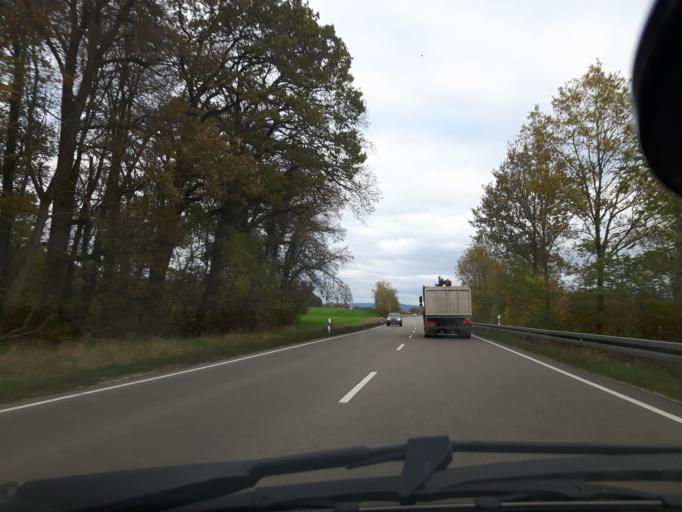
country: DE
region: Bavaria
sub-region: Regierungsbezirk Mittelfranken
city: Weidenbach
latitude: 49.2103
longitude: 10.6534
